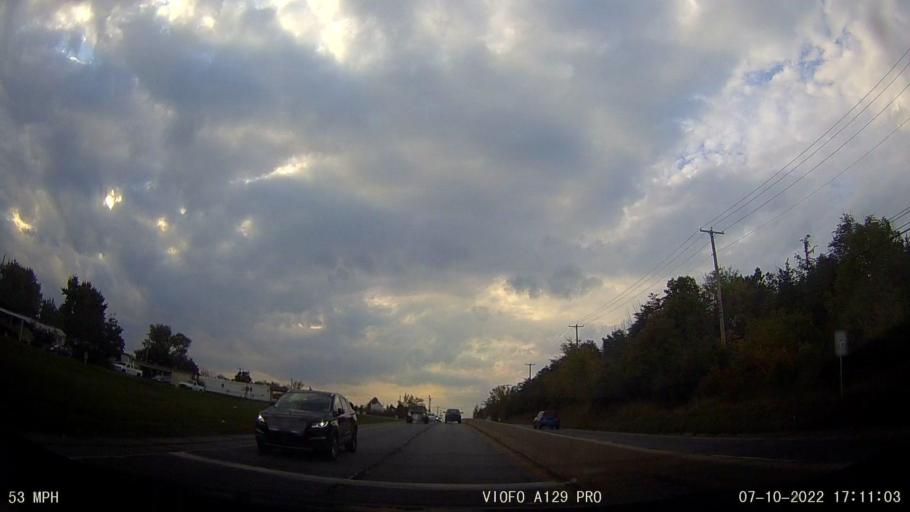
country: US
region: Pennsylvania
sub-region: Berks County
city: Amity Gardens
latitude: 40.2659
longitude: -75.7555
